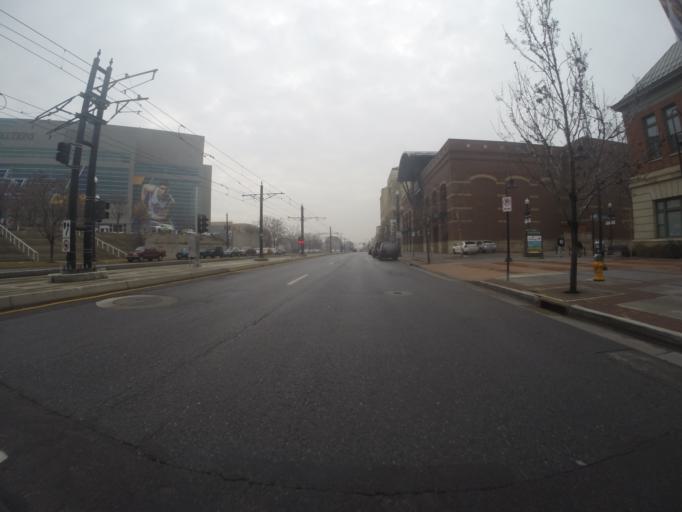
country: US
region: Utah
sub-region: Salt Lake County
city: Salt Lake City
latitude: 40.7690
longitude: -111.9027
